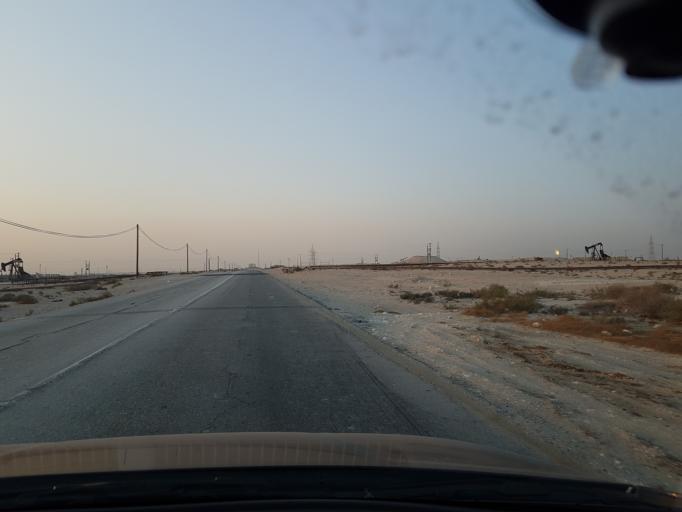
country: BH
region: Central Governorate
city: Dar Kulayb
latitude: 26.0618
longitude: 50.5539
